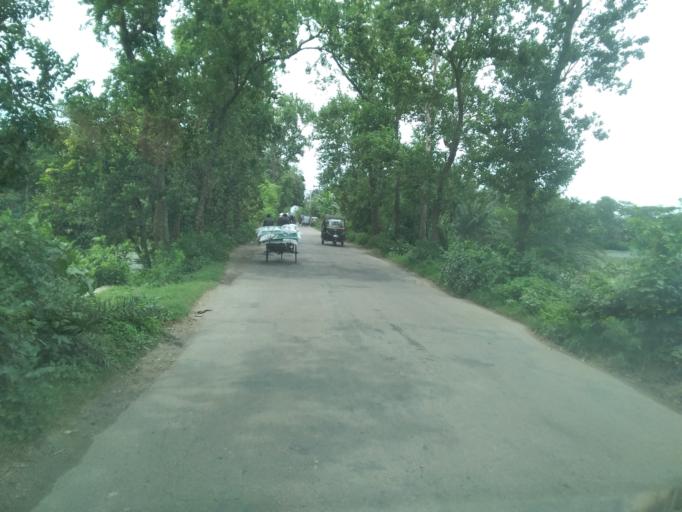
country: IN
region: West Bengal
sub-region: North 24 Parganas
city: Taki
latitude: 22.5754
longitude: 88.9993
